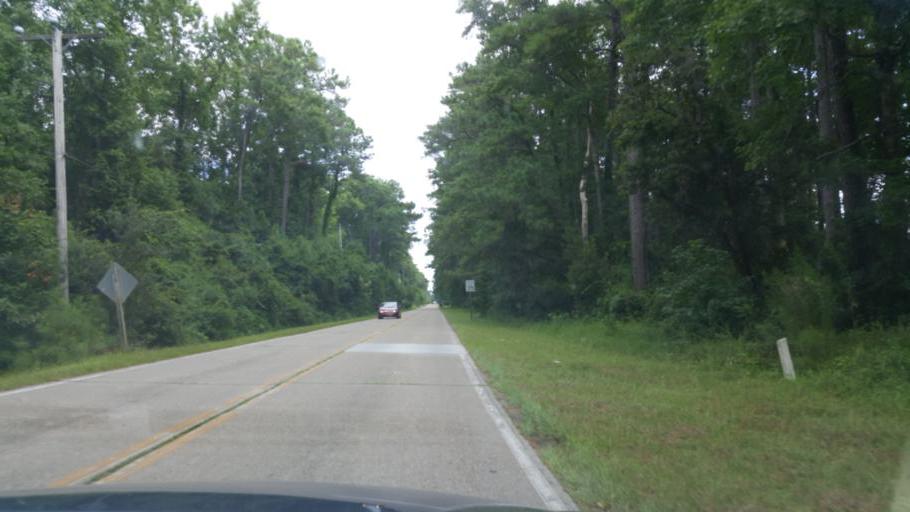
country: US
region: North Carolina
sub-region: Dare County
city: Manteo
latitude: 35.9222
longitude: -75.7057
